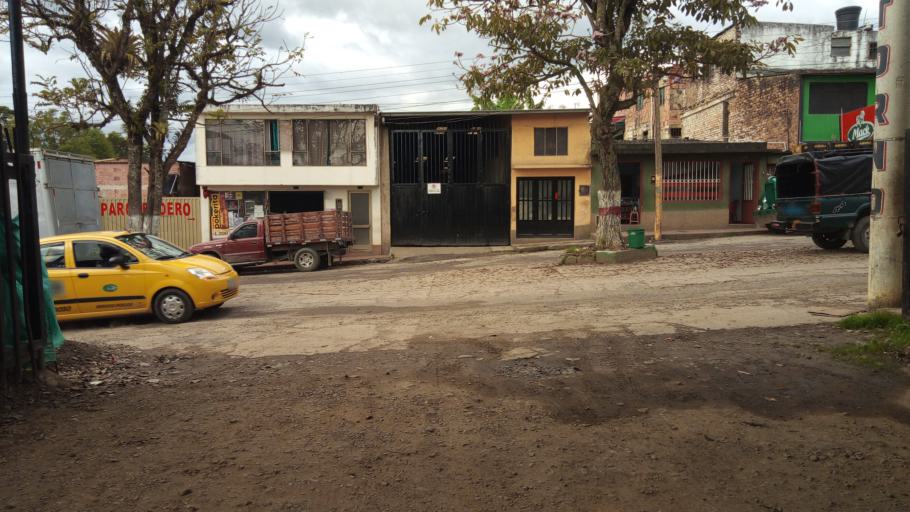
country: CO
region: Boyaca
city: Garagoa
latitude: 5.0859
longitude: -73.3647
